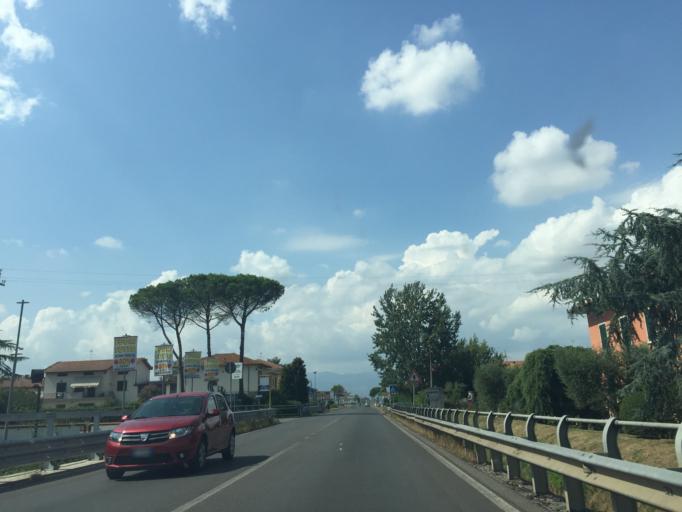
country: IT
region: Tuscany
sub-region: Provincia di Pistoia
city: Barba
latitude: 43.8740
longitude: 10.9820
